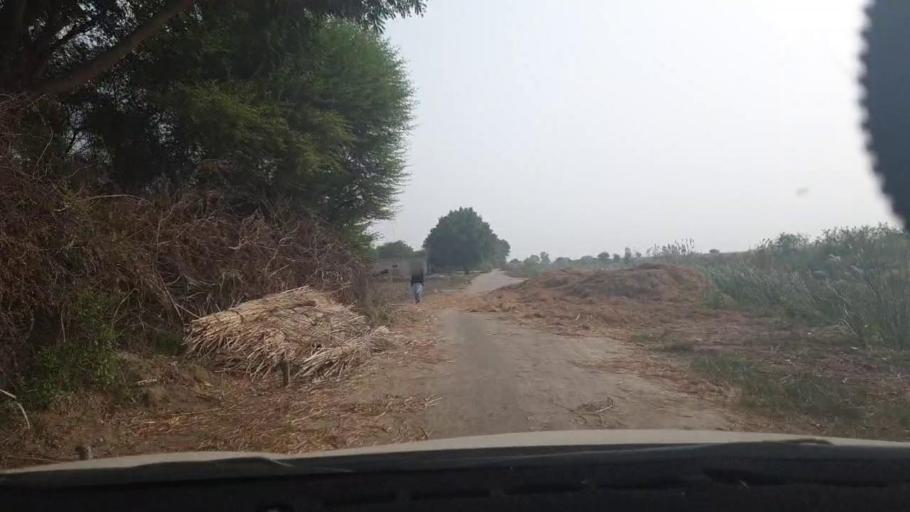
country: PK
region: Sindh
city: Tando Muhammad Khan
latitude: 24.9728
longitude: 68.4855
